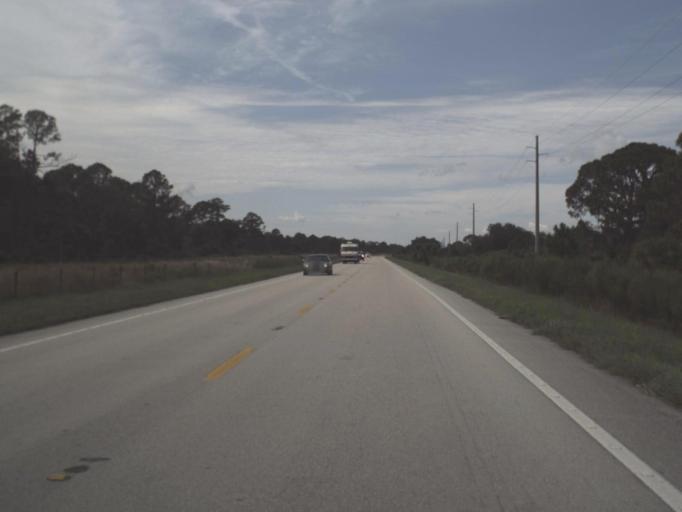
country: US
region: Florida
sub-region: Highlands County
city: Placid Lakes
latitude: 27.2092
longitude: -81.4665
